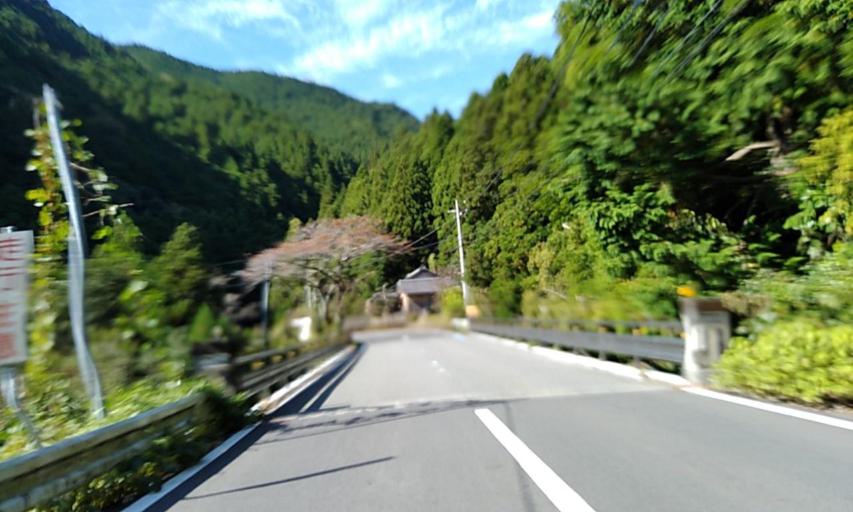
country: JP
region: Wakayama
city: Kainan
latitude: 34.0846
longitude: 135.3564
